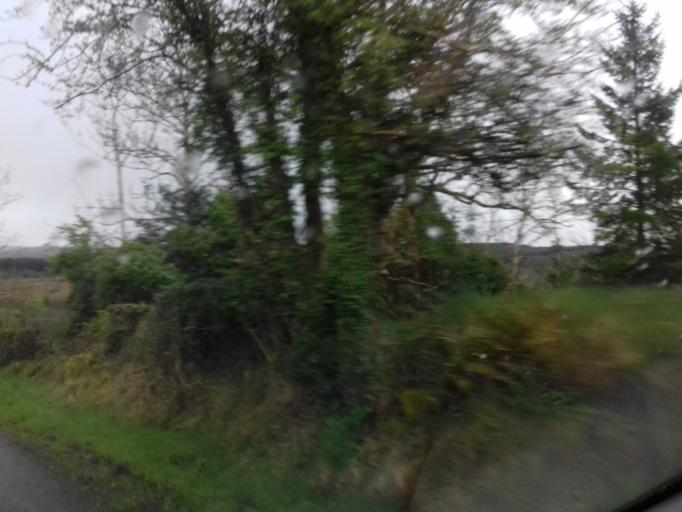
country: IE
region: Connaught
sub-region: County Leitrim
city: Manorhamilton
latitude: 54.2819
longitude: -7.9379
